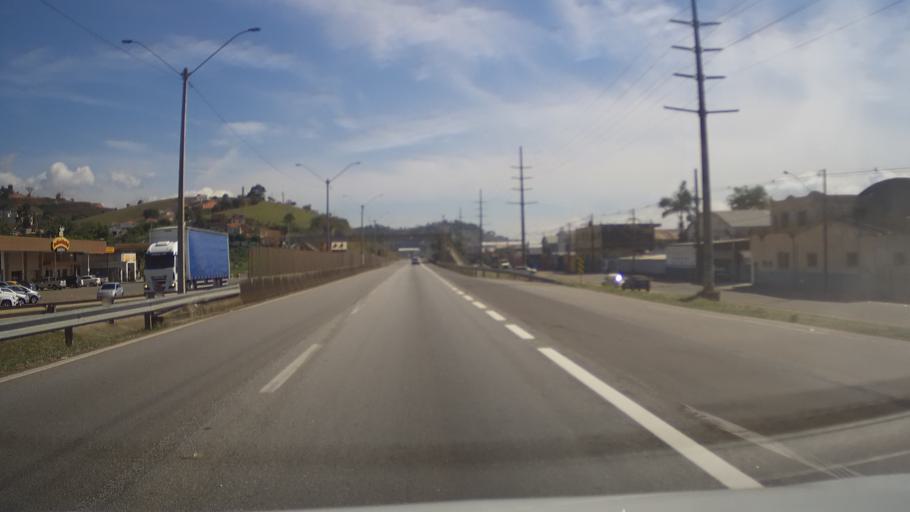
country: BR
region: Minas Gerais
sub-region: Cambui
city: Cambui
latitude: -22.6069
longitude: -46.0601
